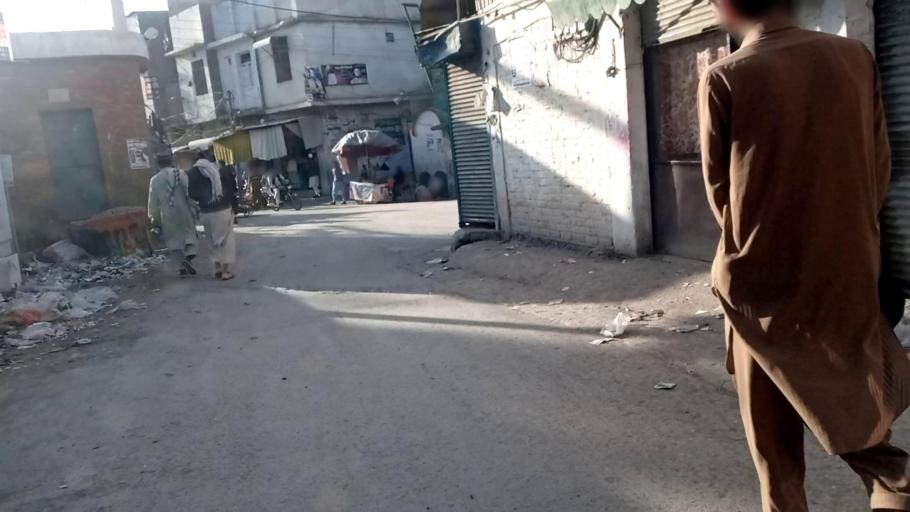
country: PK
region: Khyber Pakhtunkhwa
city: Peshawar
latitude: 34.0069
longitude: 71.5963
